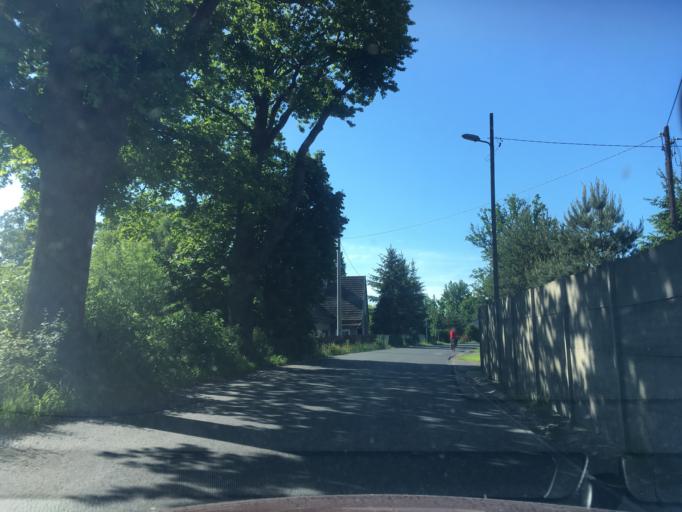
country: PL
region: Lower Silesian Voivodeship
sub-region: Powiat zgorzelecki
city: Sulikow
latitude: 51.0821
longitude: 15.0567
